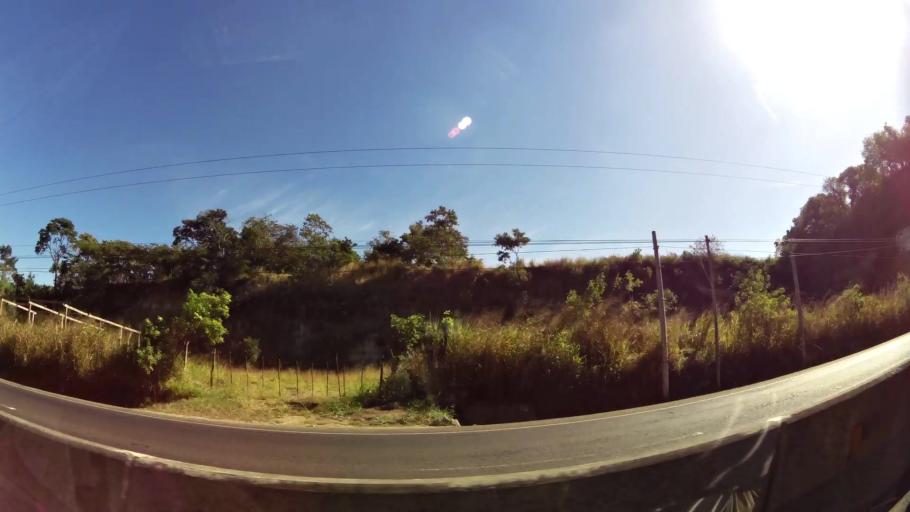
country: SV
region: Santa Ana
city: Coatepeque
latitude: 13.9321
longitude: -89.5229
